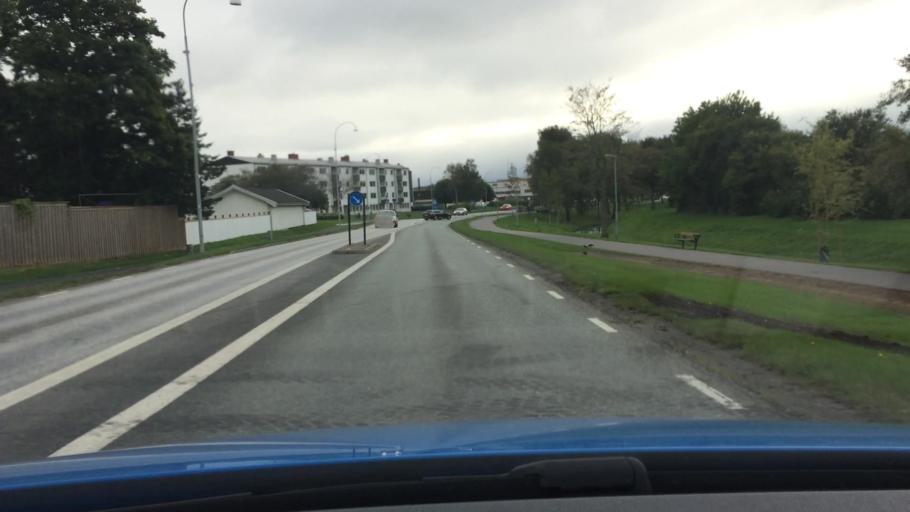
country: SE
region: Halland
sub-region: Kungsbacka Kommun
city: Kungsbacka
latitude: 57.4886
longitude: 12.0878
